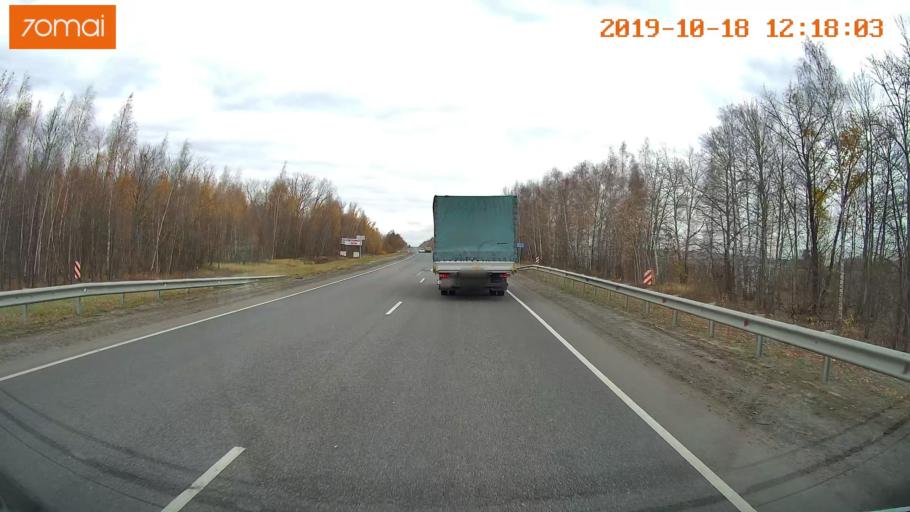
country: RU
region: Rjazan
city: Zakharovo
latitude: 54.4627
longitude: 39.4525
